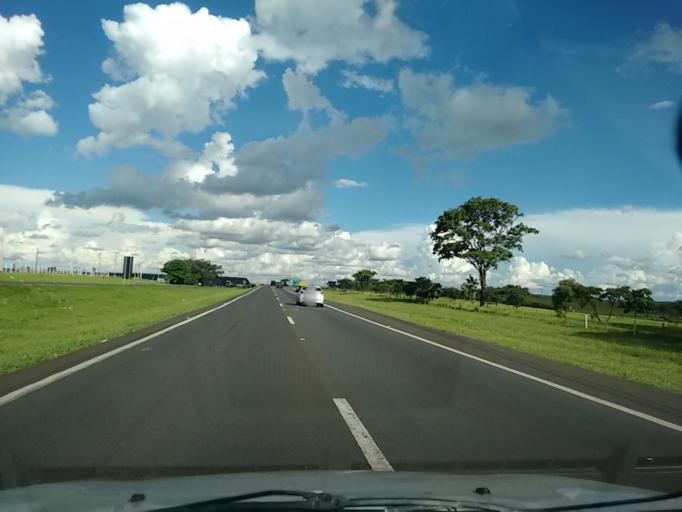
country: BR
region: Sao Paulo
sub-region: Ibate
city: Ibate
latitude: -21.9380
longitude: -48.0104
